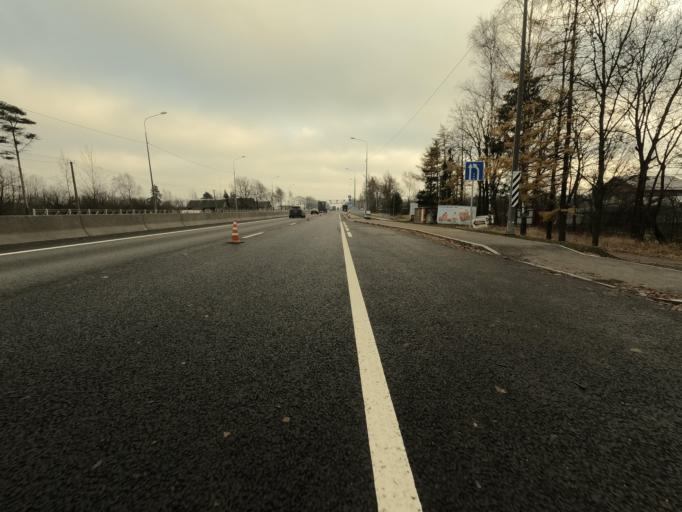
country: RU
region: Leningrad
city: Mga
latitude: 59.7252
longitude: 31.0949
